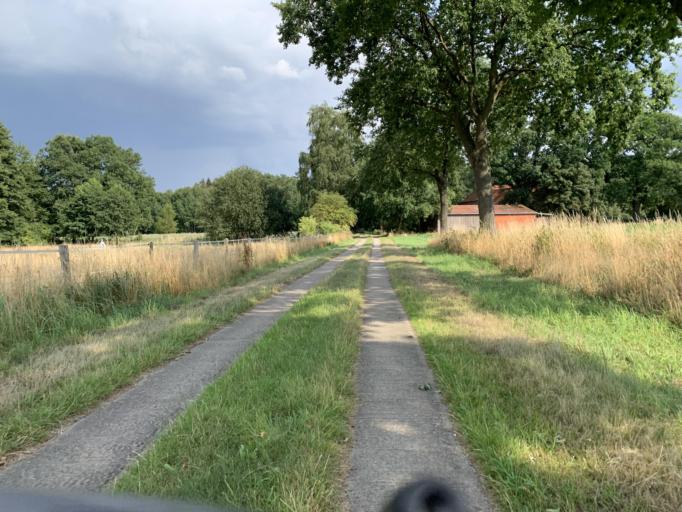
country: DE
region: Lower Saxony
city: Neetze
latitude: 53.2425
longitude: 10.6365
